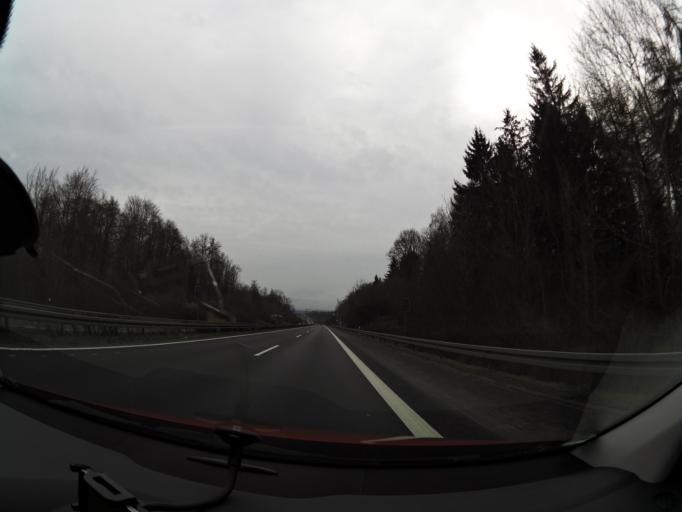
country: DE
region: Lower Saxony
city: Gielde
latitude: 52.0564
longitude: 10.5053
